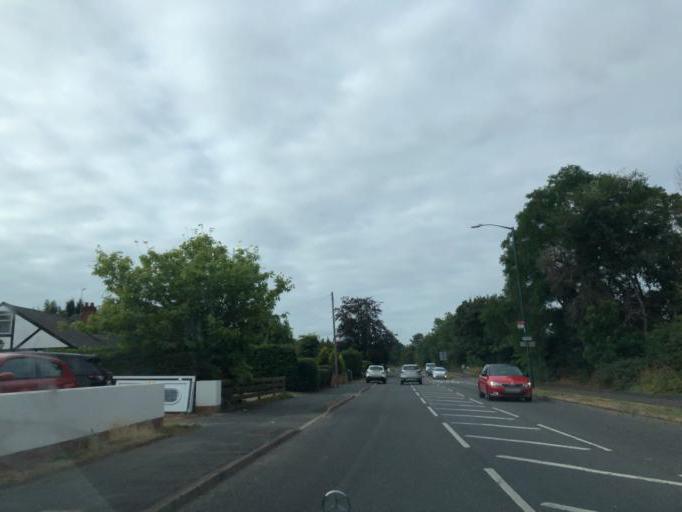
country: GB
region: England
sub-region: Warwickshire
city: Royal Leamington Spa
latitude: 52.2677
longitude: -1.5344
